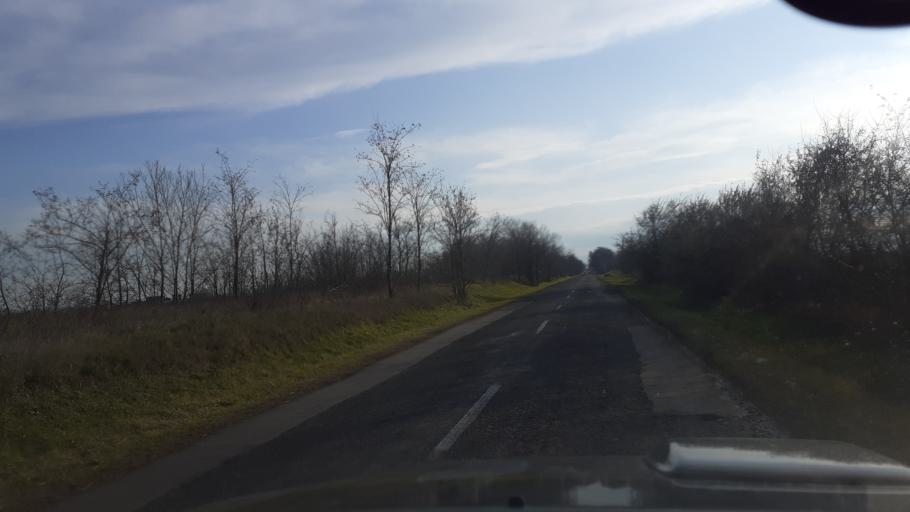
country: HU
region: Pest
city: Domsod
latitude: 47.1027
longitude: 19.0915
